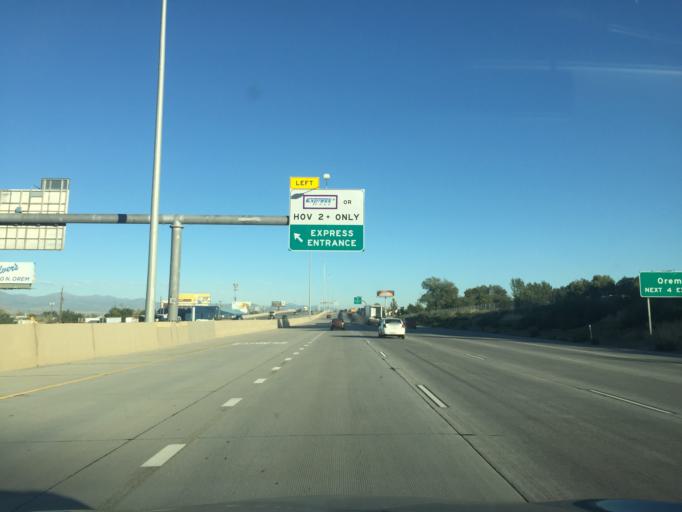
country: US
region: Utah
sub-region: Utah County
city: Orem
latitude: 40.2570
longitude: -111.7012
